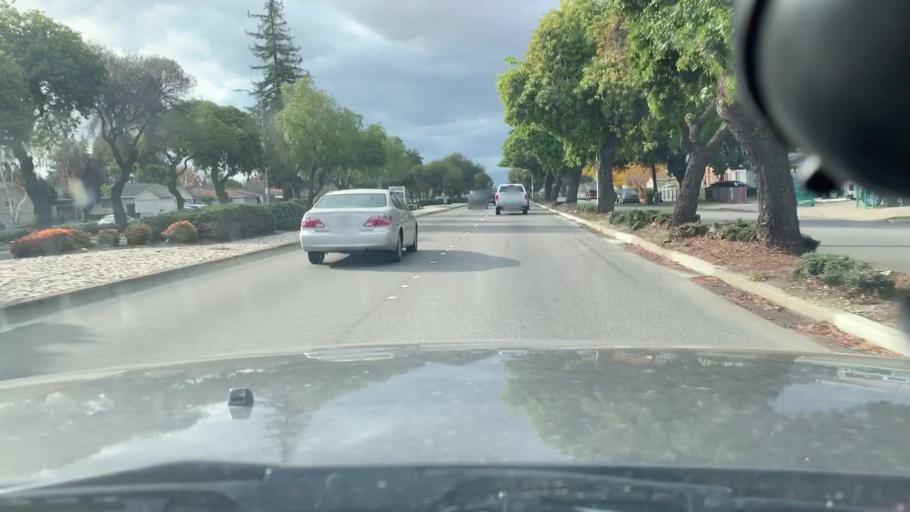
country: US
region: California
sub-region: Alameda County
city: Fremont
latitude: 37.5325
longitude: -121.9798
